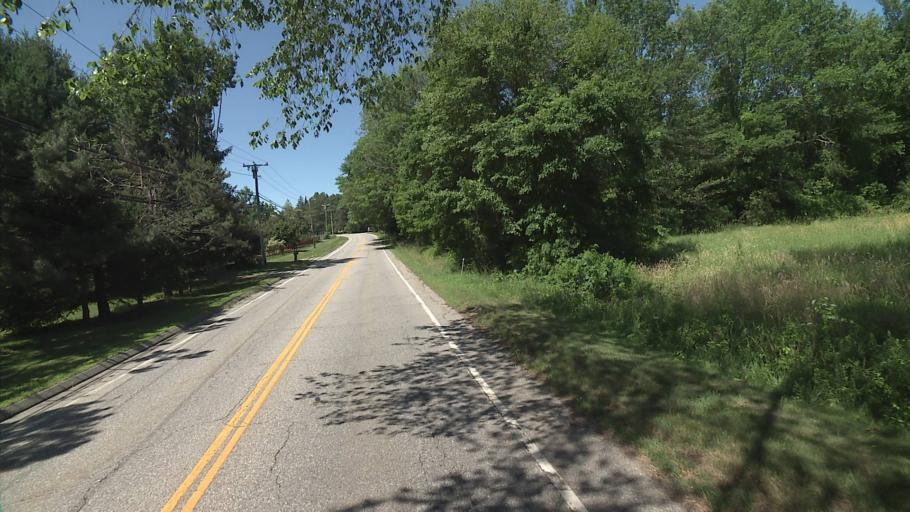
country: US
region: Connecticut
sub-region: Windham County
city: Willimantic
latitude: 41.6850
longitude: -72.2355
